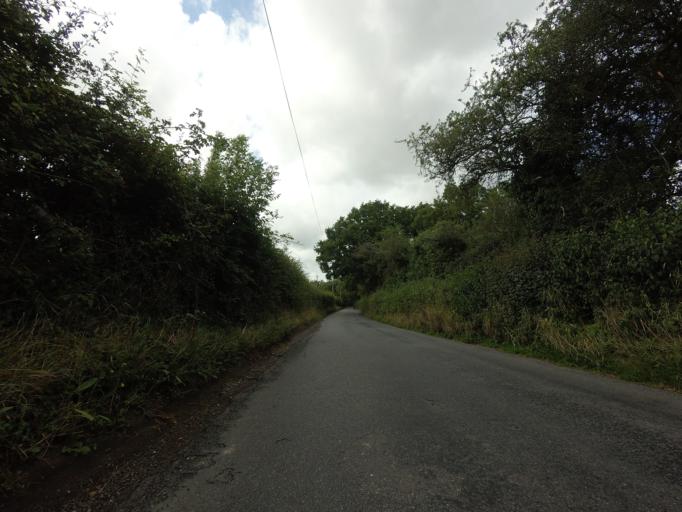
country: GB
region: England
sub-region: Kent
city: Hadlow
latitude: 51.2390
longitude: 0.3251
